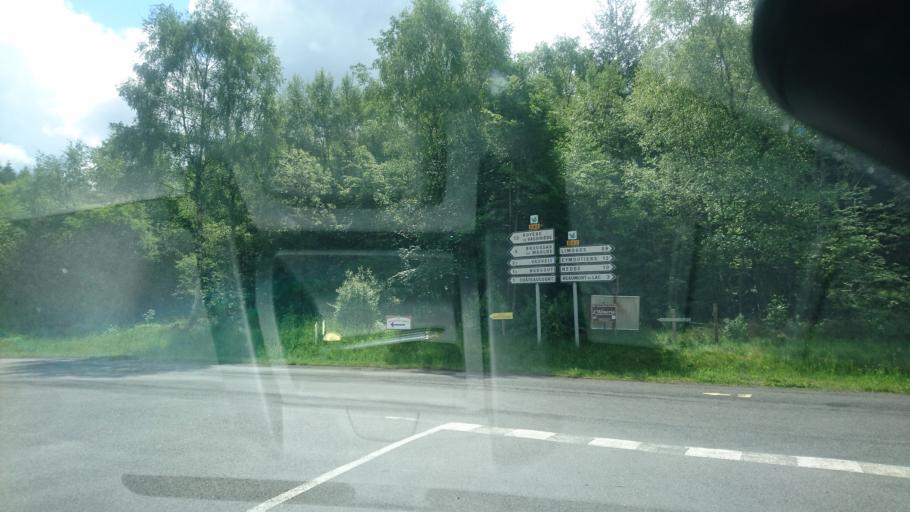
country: FR
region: Limousin
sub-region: Departement de la Haute-Vienne
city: Peyrat-le-Chateau
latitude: 45.7751
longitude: 1.8706
